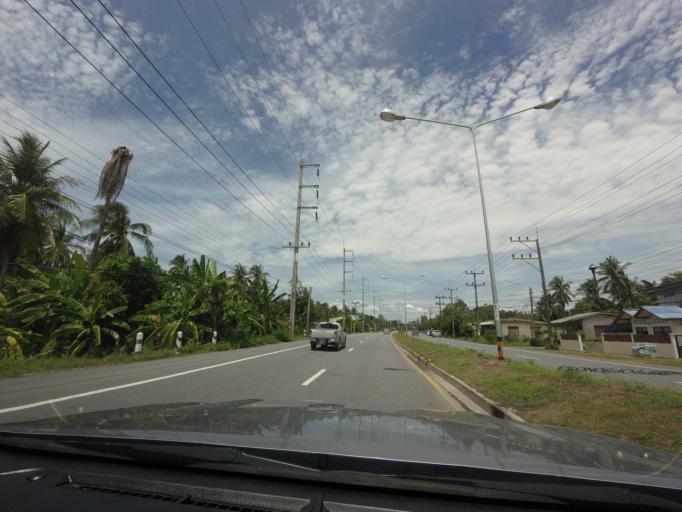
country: TH
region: Songkhla
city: Krasae Sin
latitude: 7.5781
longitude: 100.4084
